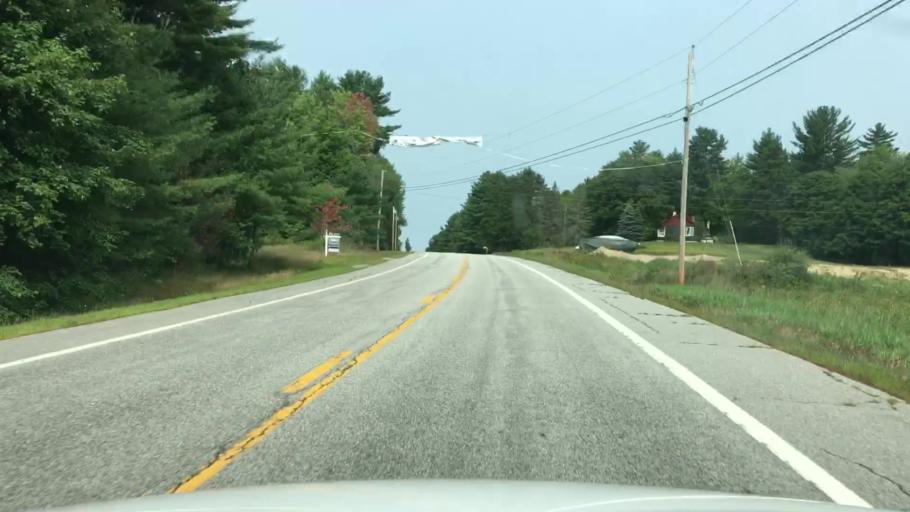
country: US
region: Maine
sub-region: Kennebec County
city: Wayne
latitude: 44.3955
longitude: -70.1178
